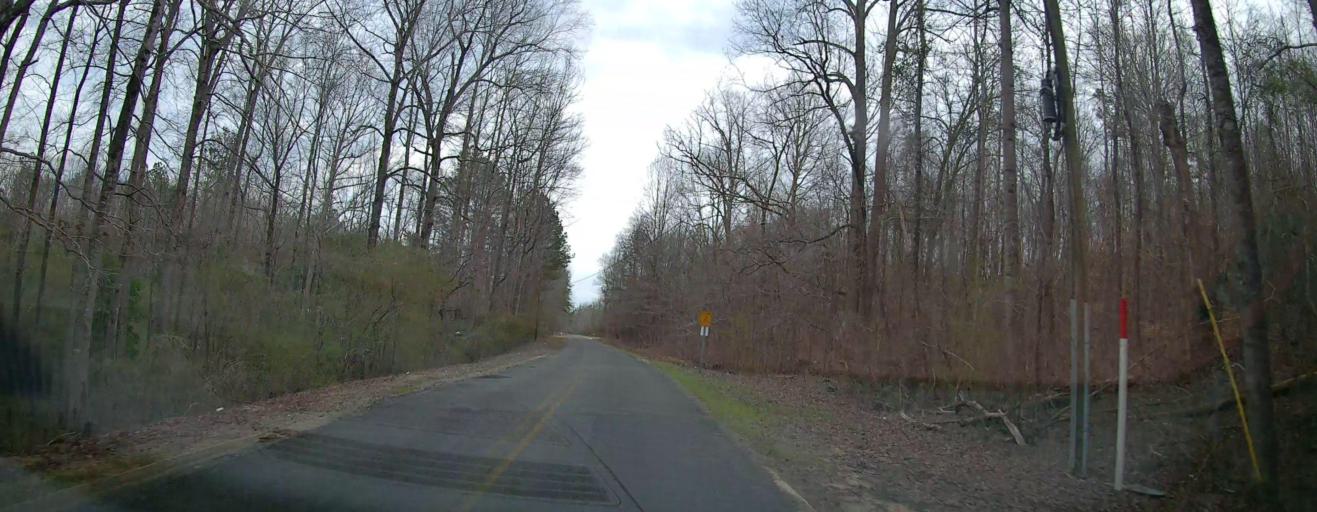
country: US
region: Alabama
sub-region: Marion County
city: Hamilton
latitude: 34.2028
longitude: -88.1904
